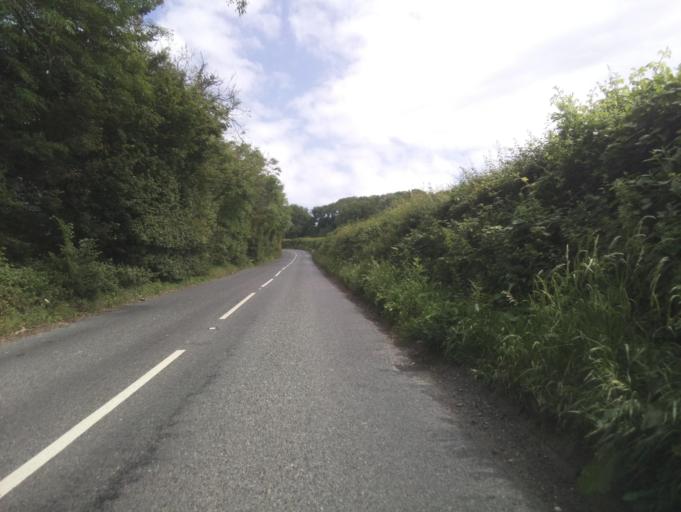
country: GB
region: England
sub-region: Somerset
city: Milborne Port
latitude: 51.0129
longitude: -2.4728
